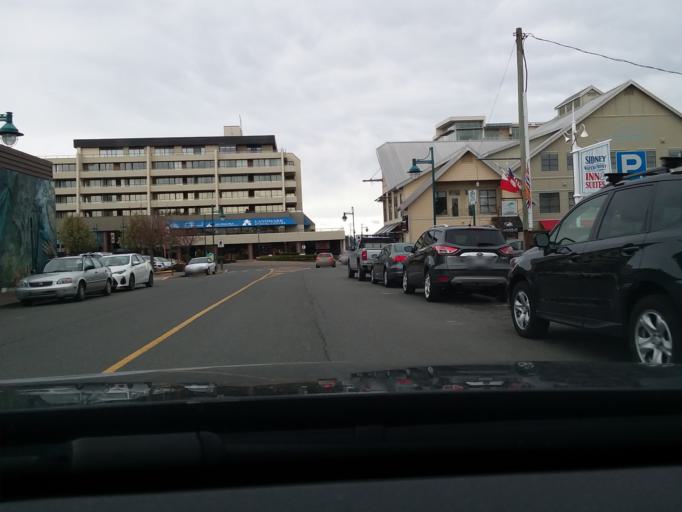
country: CA
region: British Columbia
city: North Saanich
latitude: 48.6482
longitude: -123.3953
